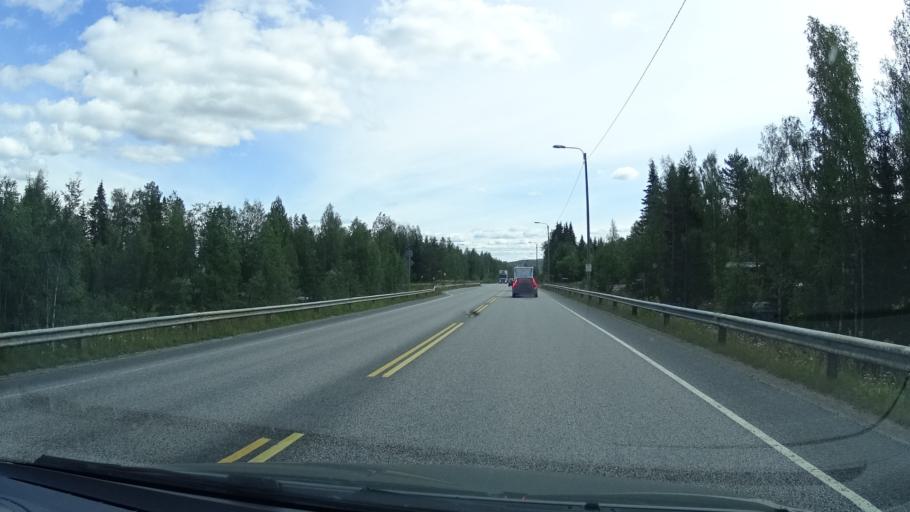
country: FI
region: Central Finland
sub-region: Jyvaeskylae
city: Jyvaeskylae
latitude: 62.2607
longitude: 25.5973
